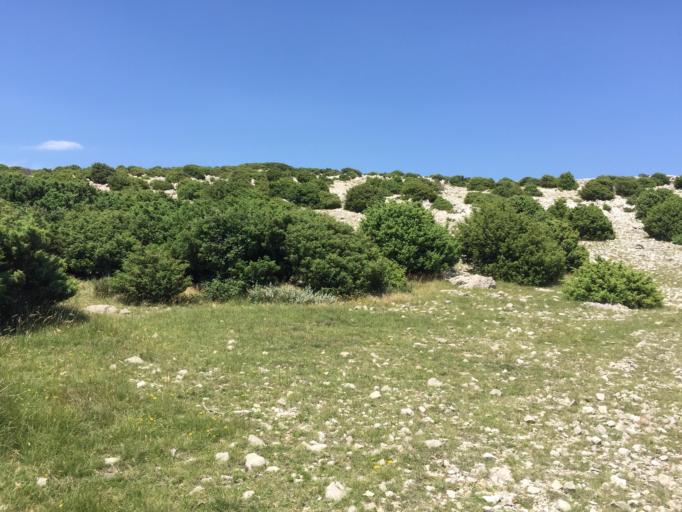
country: HR
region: Primorsko-Goranska
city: Punat
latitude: 45.0089
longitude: 14.6821
